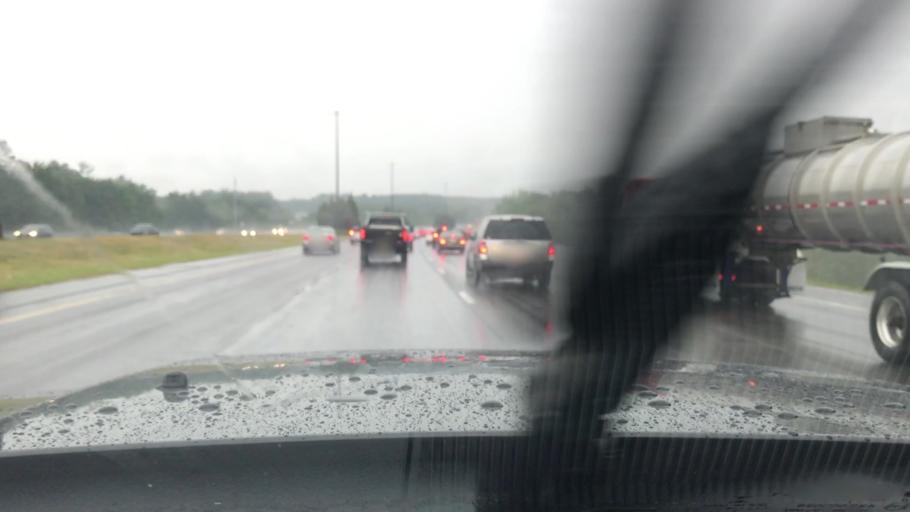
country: US
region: New Hampshire
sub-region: Rockingham County
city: Greenland
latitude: 43.0521
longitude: -70.8105
